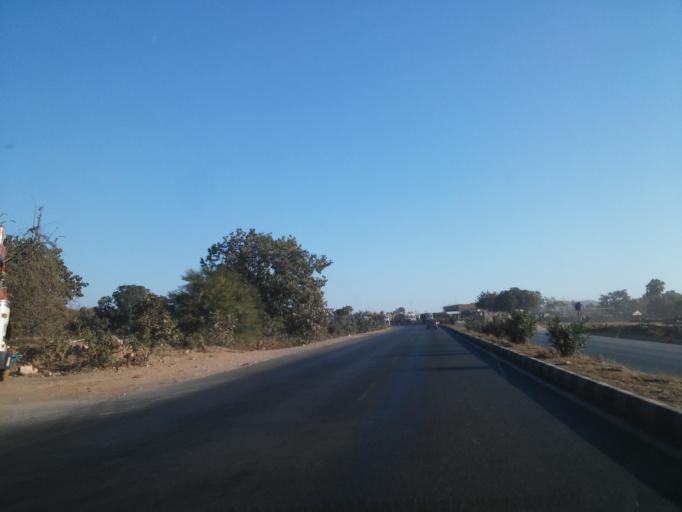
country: IN
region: Rajasthan
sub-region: Dungarpur
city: Dungarpur
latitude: 23.9512
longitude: 73.5783
